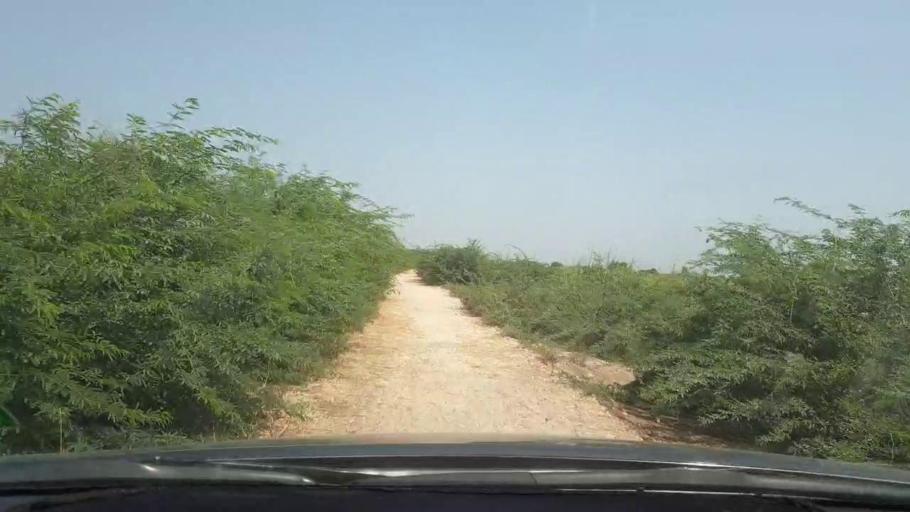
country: PK
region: Sindh
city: Tando Bago
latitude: 24.7771
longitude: 69.1879
